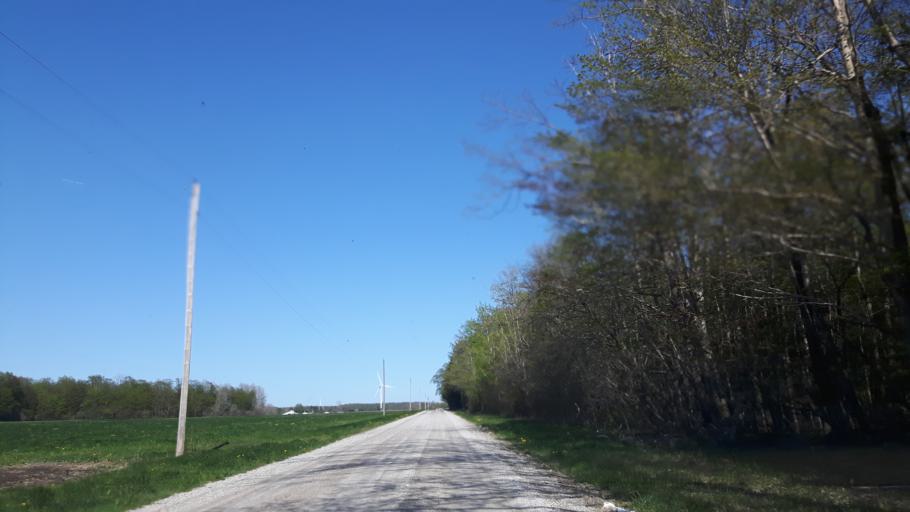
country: CA
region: Ontario
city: Bluewater
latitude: 43.5096
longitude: -81.6881
